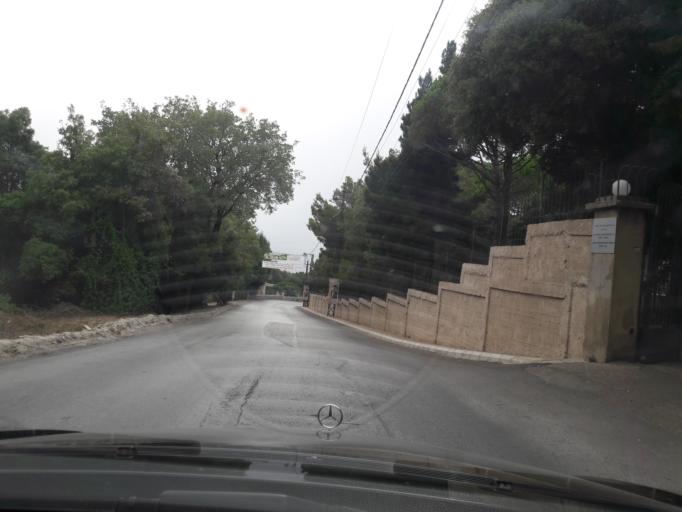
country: LB
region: Mont-Liban
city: Djounie
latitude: 33.9885
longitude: 35.6849
